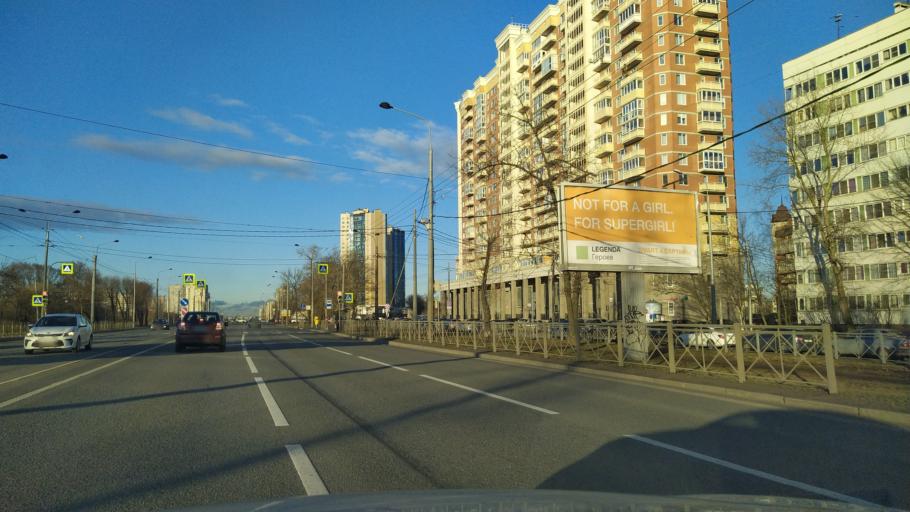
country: RU
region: St.-Petersburg
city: Uritsk
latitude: 59.8409
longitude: 30.2055
